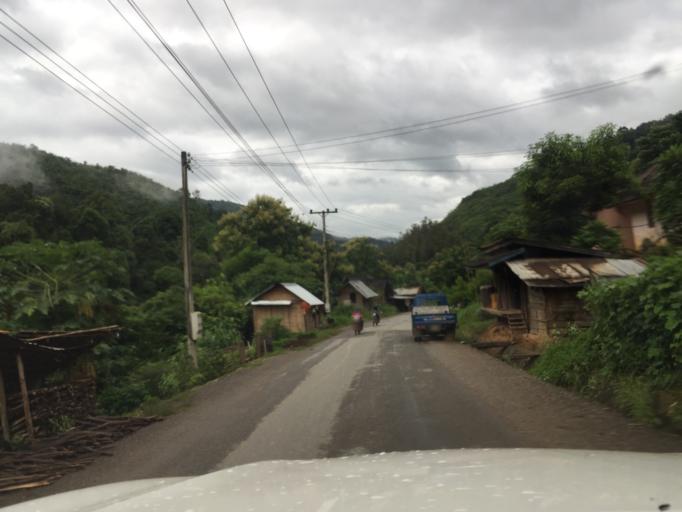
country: LA
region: Oudomxai
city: Muang La
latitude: 20.9806
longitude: 102.2250
